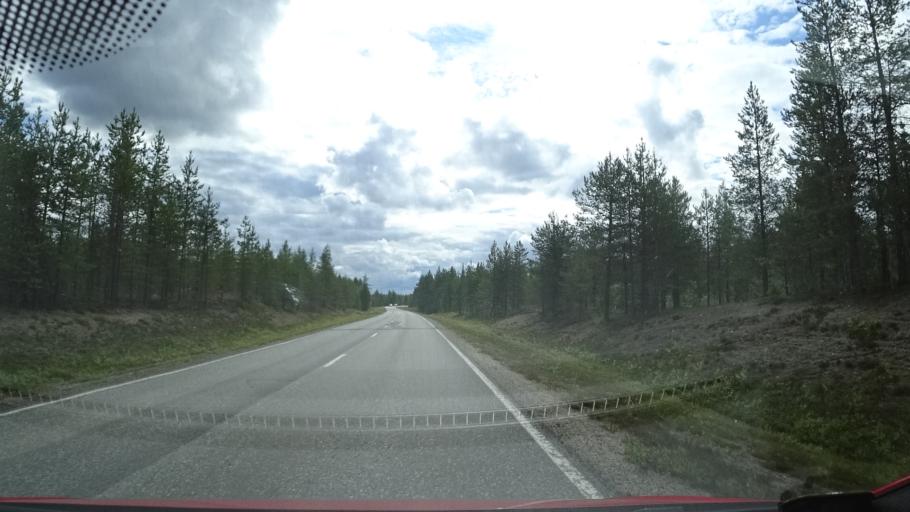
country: FI
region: Lapland
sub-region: Tunturi-Lappi
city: Kittilae
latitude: 67.5067
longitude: 24.8988
